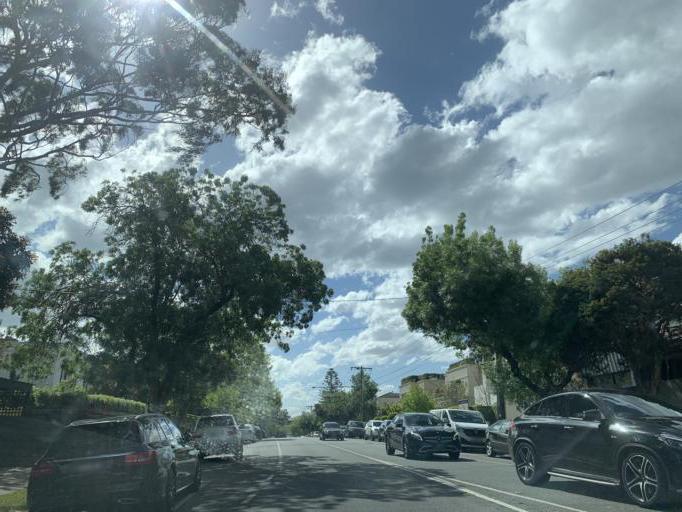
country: AU
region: Victoria
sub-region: Bayside
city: North Brighton
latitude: -37.9148
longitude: 144.9935
